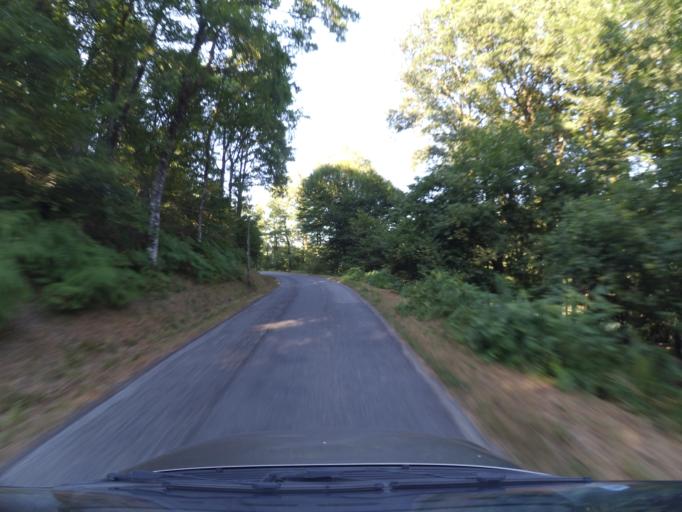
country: FR
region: Limousin
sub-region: Departement de la Haute-Vienne
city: Eymoutiers
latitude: 45.7239
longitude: 1.8256
